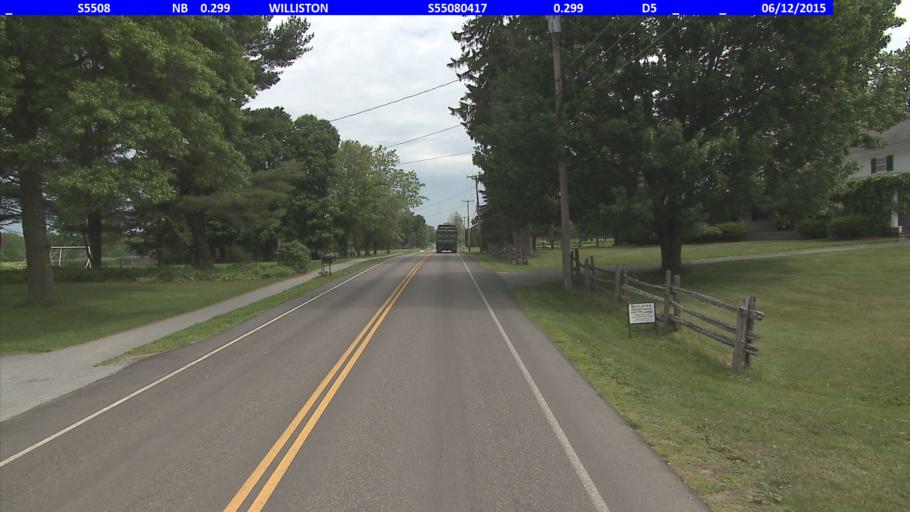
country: US
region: Vermont
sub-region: Chittenden County
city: Williston
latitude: 44.4412
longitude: -73.0653
